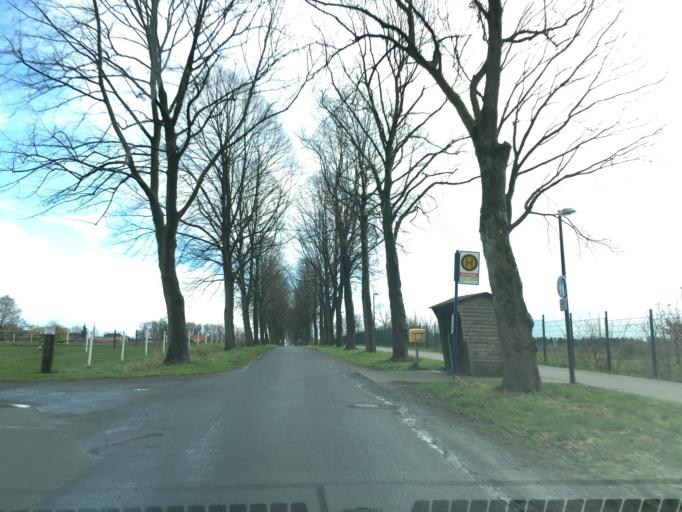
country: DE
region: North Rhine-Westphalia
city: Olfen
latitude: 51.7584
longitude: 7.3845
